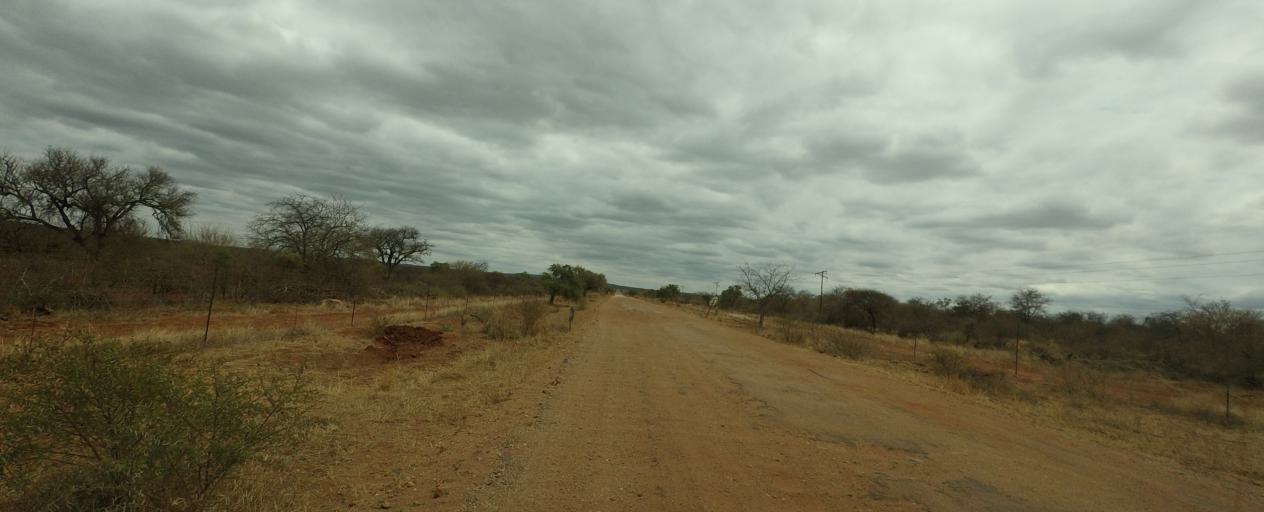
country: BW
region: Central
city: Mathathane
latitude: -22.7400
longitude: 28.4836
